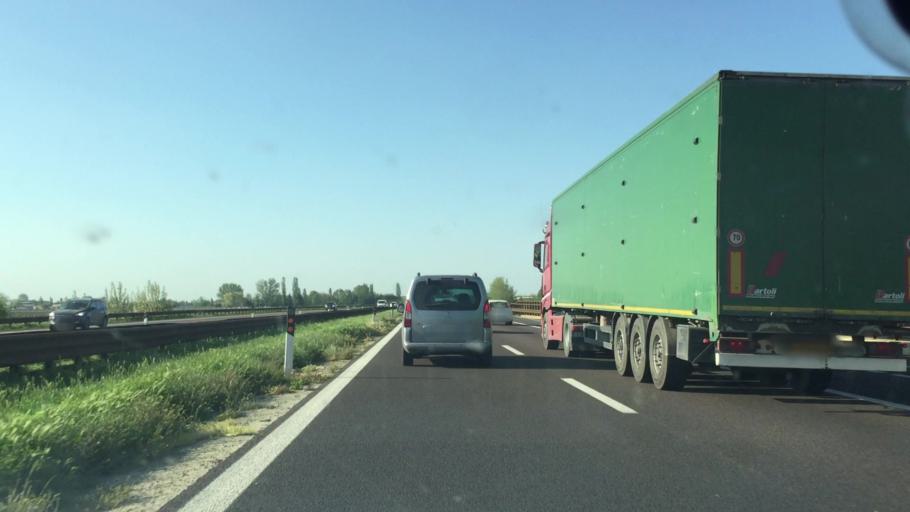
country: IT
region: Emilia-Romagna
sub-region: Provincia di Modena
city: Campogalliano
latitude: 44.7256
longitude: 10.8447
